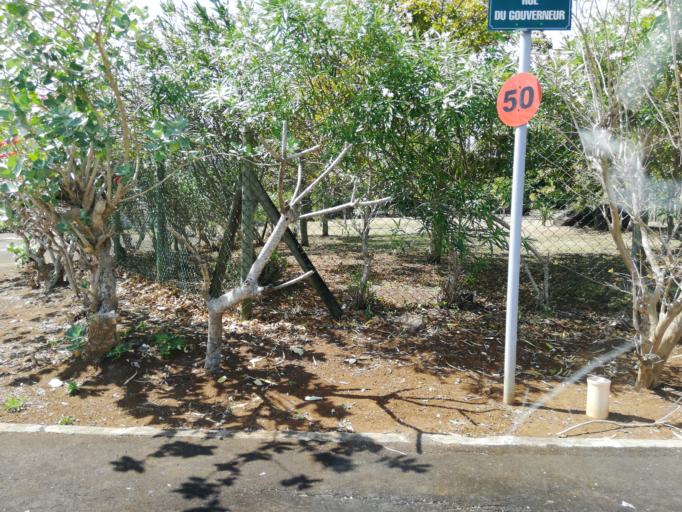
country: MU
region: Plaines Wilhems
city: Ebene
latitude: -20.2303
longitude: 57.4816
